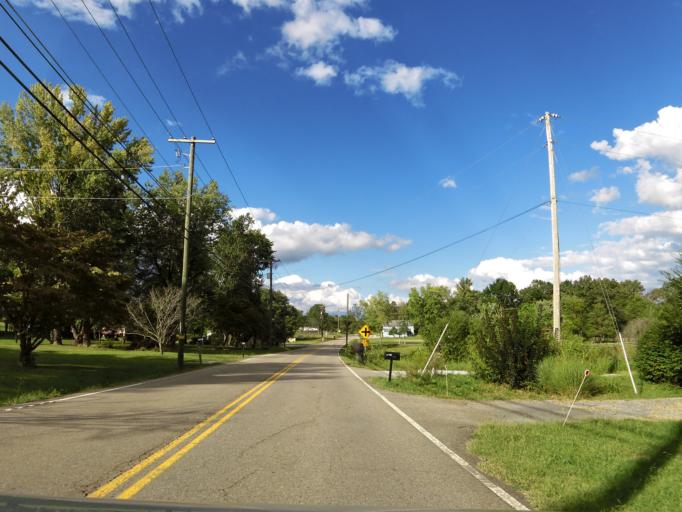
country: US
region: Tennessee
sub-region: Knox County
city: Mascot
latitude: 36.1032
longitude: -83.8141
